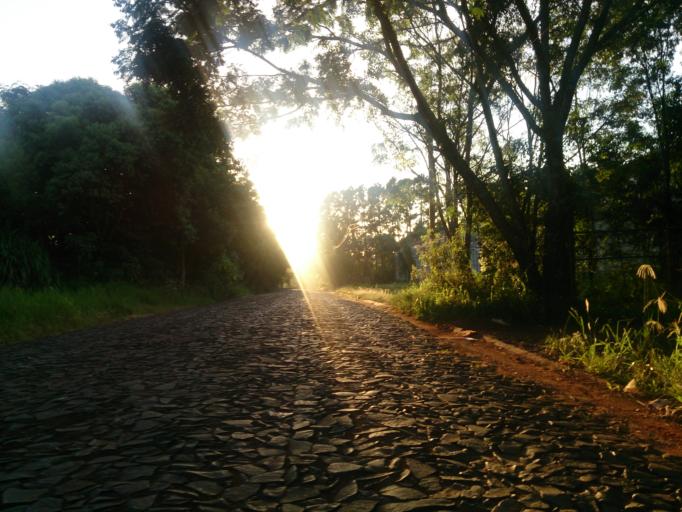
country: AR
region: Misiones
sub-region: Departamento de Obera
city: Obera
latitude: -27.4951
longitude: -55.1154
